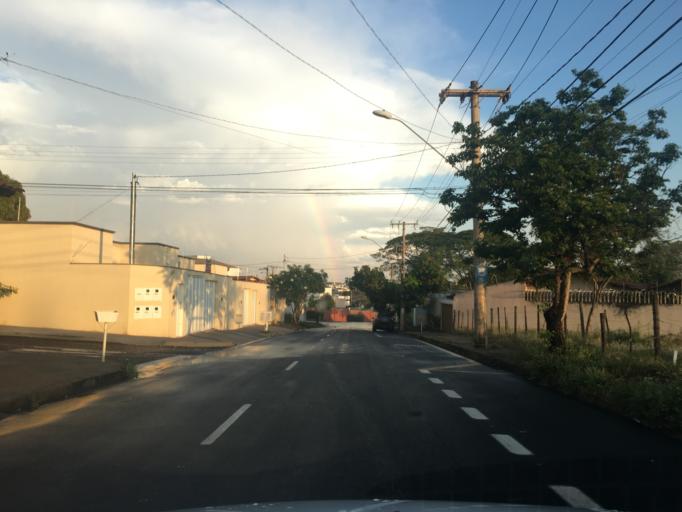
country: BR
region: Minas Gerais
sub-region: Uberlandia
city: Uberlandia
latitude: -18.9309
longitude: -48.2632
